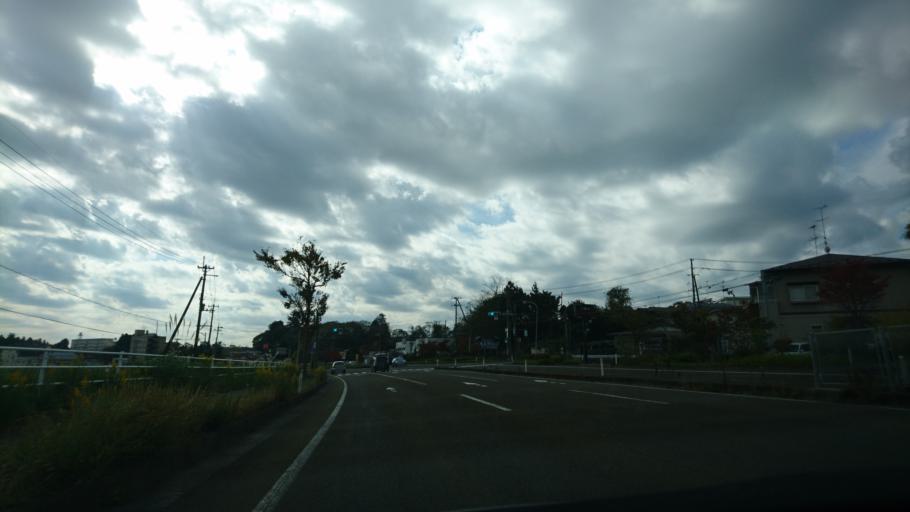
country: JP
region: Miyagi
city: Tomiya
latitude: 38.4556
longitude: 140.8791
